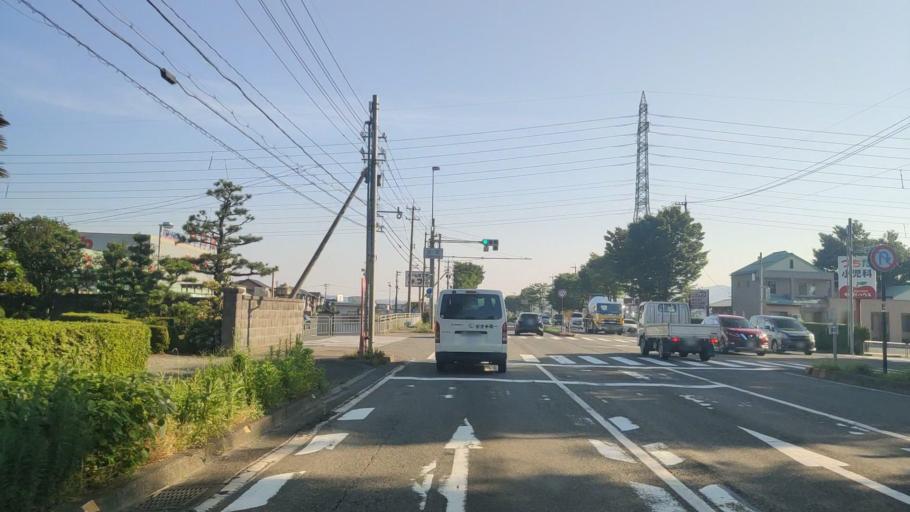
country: JP
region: Fukui
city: Maruoka
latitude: 36.1367
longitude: 136.2628
